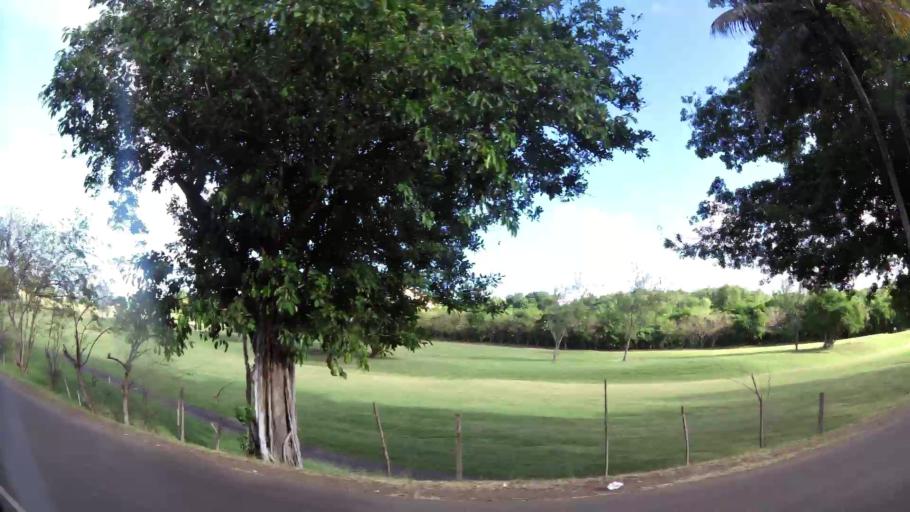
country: LC
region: Gros-Islet
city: Gros Islet
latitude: 14.0940
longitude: -60.9458
